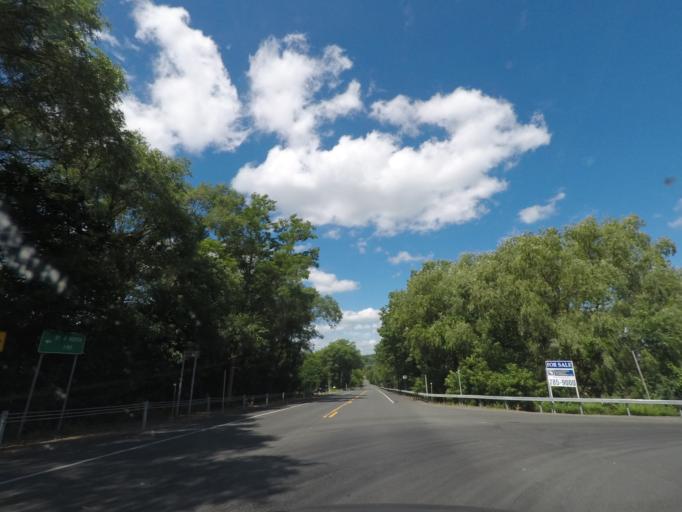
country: US
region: New York
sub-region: Rensselaer County
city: Hampton Manor
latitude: 42.6198
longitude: -73.7043
